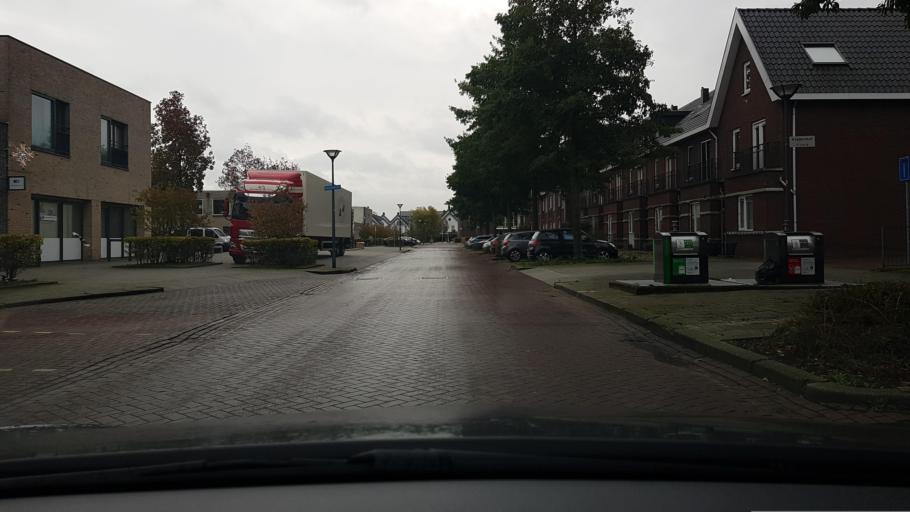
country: NL
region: North Holland
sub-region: Gemeente Bloemendaal
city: Bennebroek
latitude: 52.3064
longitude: 4.6370
